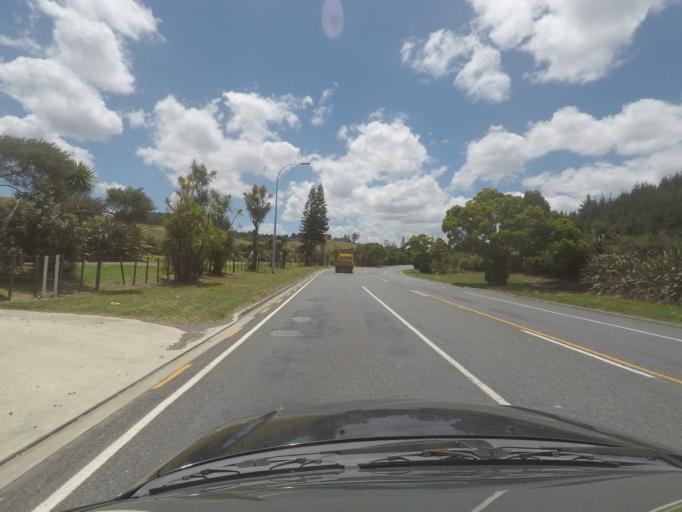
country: NZ
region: Northland
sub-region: Whangarei
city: Whangarei
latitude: -35.7495
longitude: 174.3204
